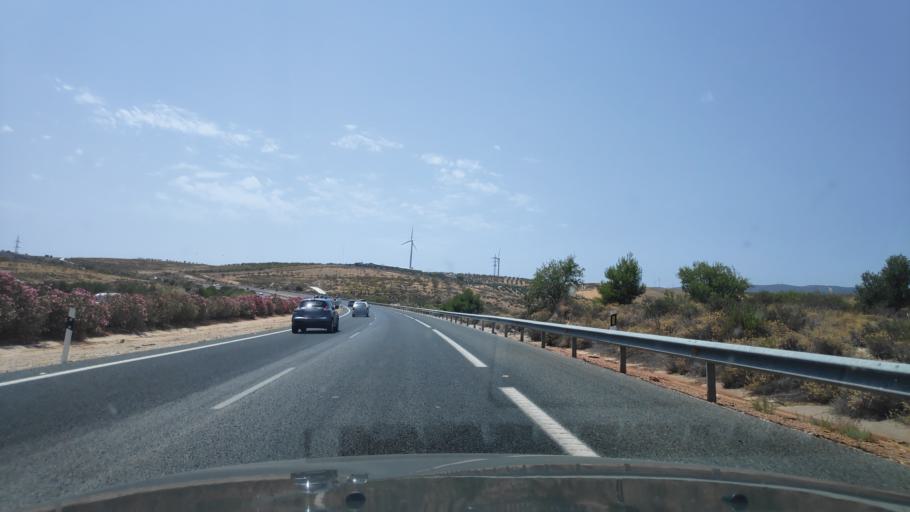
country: ES
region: Andalusia
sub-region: Provincia de Granada
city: Padul
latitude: 37.0127
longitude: -3.6405
